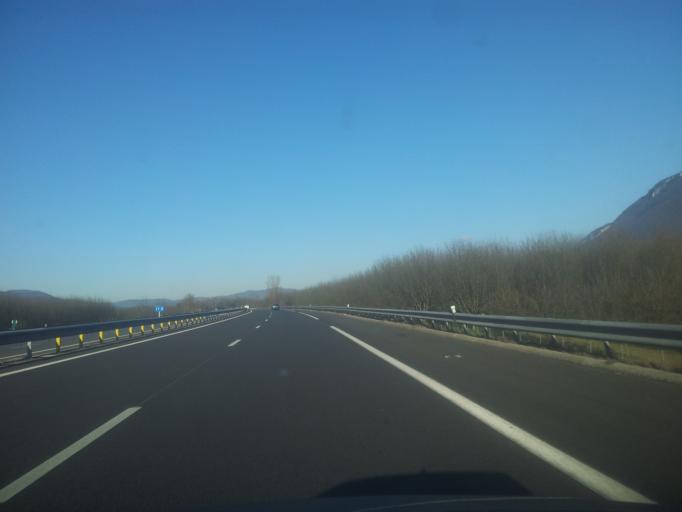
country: FR
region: Rhone-Alpes
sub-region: Departement de l'Isere
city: Vinay
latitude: 45.2216
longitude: 5.4802
